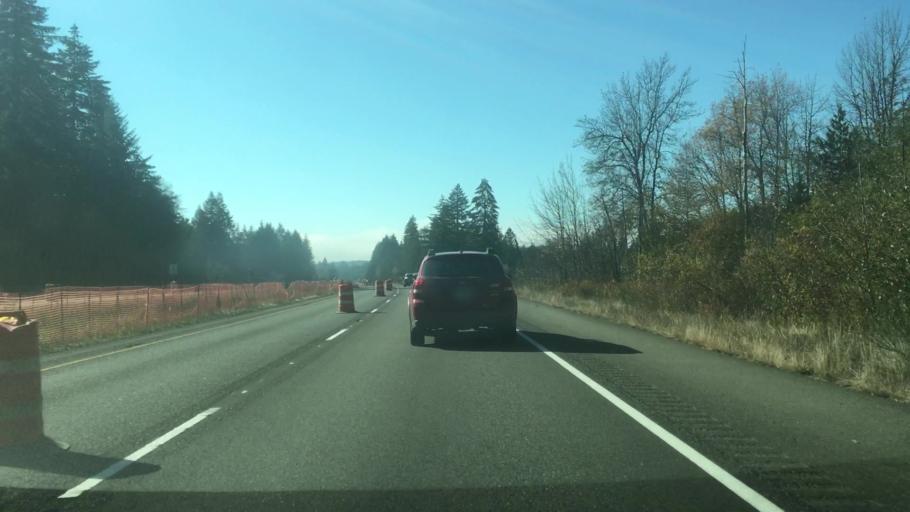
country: US
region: Washington
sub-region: Grays Harbor County
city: McCleary
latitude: 47.0539
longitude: -123.2890
